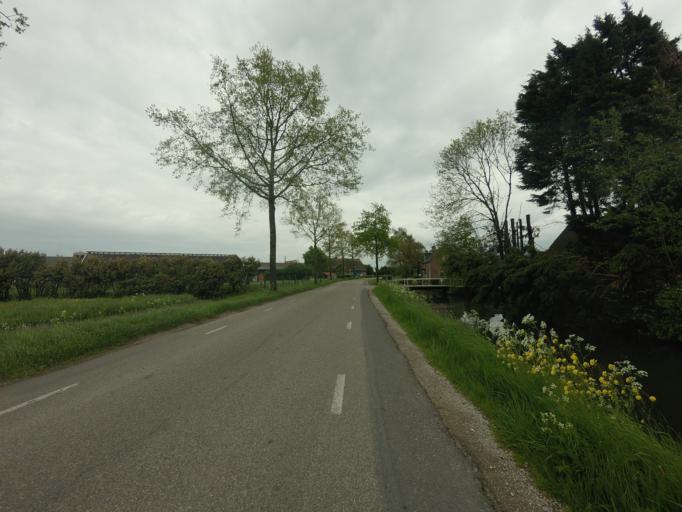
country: NL
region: Utrecht
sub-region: Gemeente IJsselstein
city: IJsselstein
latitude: 51.9881
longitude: 5.0259
